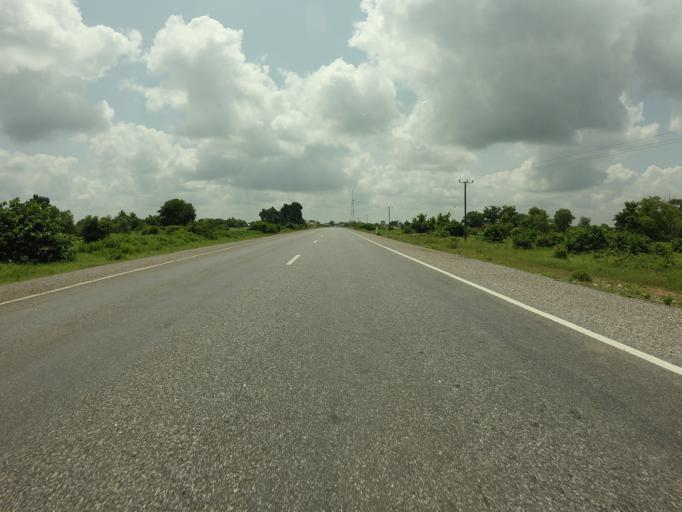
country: GH
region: Northern
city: Tamale
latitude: 9.1612
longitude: -1.5169
